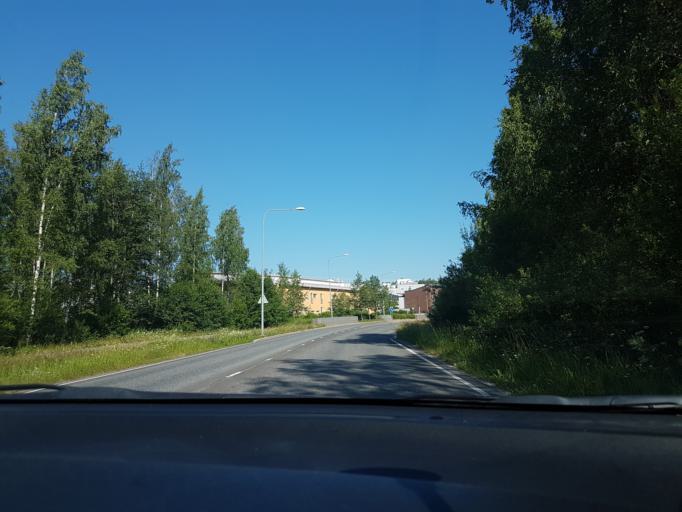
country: FI
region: Uusimaa
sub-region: Helsinki
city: Vantaa
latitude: 60.2279
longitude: 25.1350
